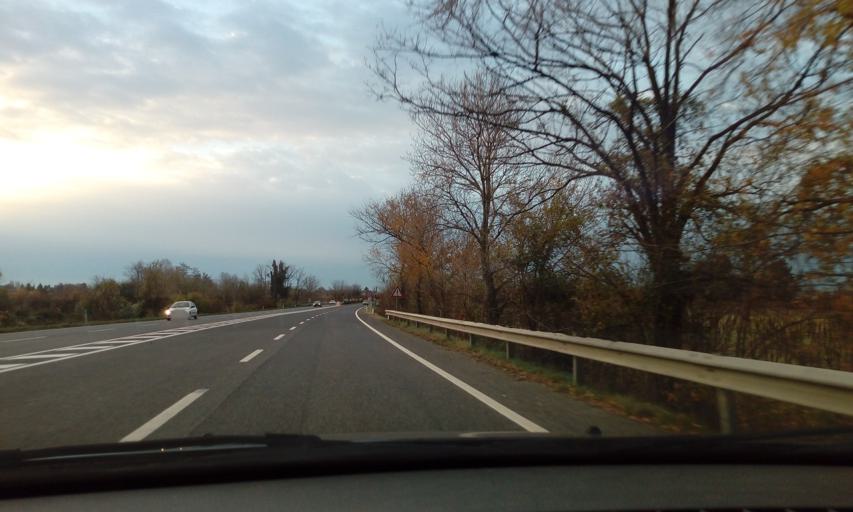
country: IT
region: Friuli Venezia Giulia
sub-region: Provincia di Gorizia
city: Ronchi dei Legionari
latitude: 45.8317
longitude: 13.4924
